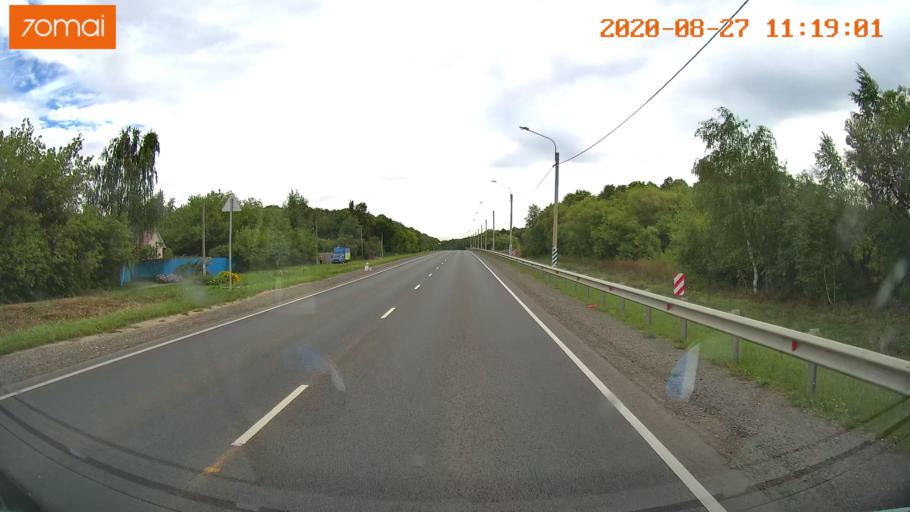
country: RU
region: Rjazan
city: Oktyabr'skiy
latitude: 54.1814
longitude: 38.9084
